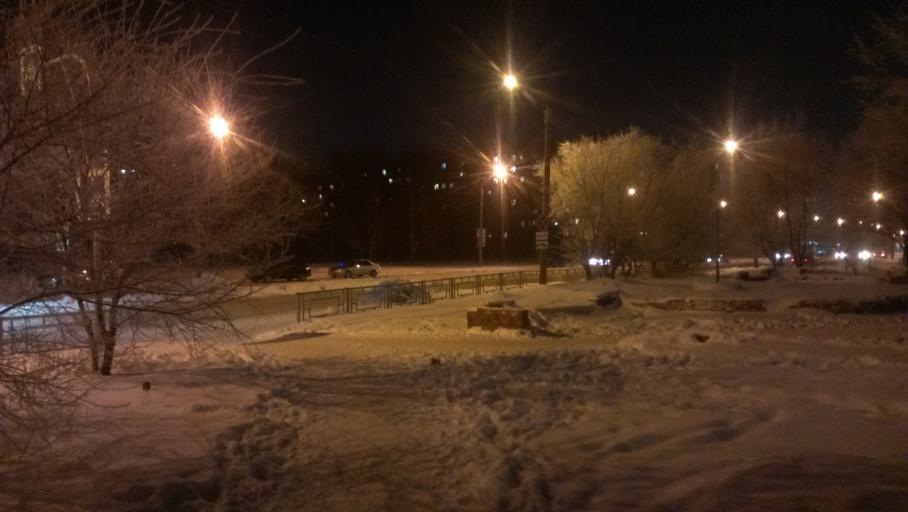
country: RU
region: Altai Krai
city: Novosilikatnyy
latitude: 53.3622
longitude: 83.6680
